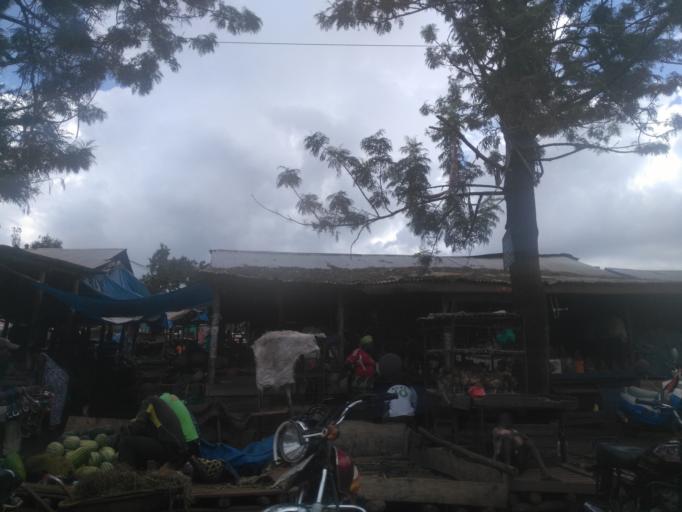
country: UG
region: Central Region
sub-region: Wakiso District
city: Kireka
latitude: 0.3452
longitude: 32.6439
